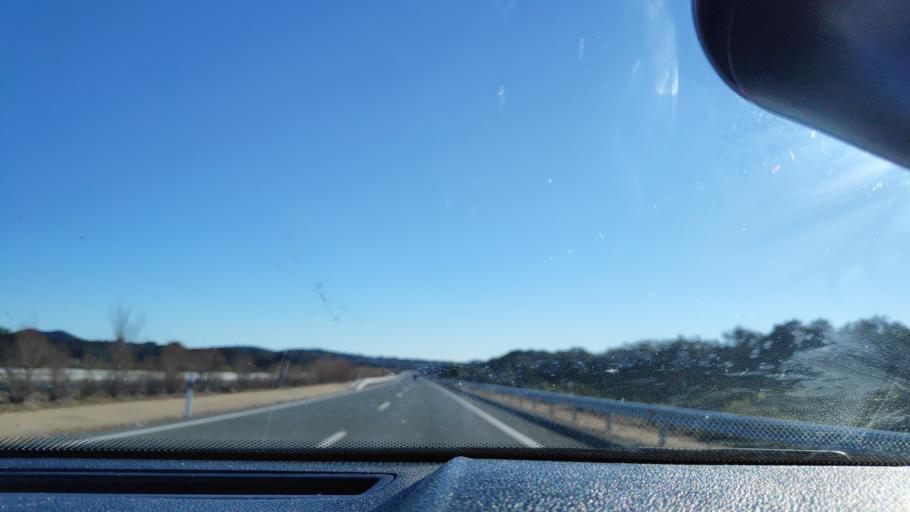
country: ES
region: Andalusia
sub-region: Provincia de Huelva
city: Cala
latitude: 37.9953
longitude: -6.2333
